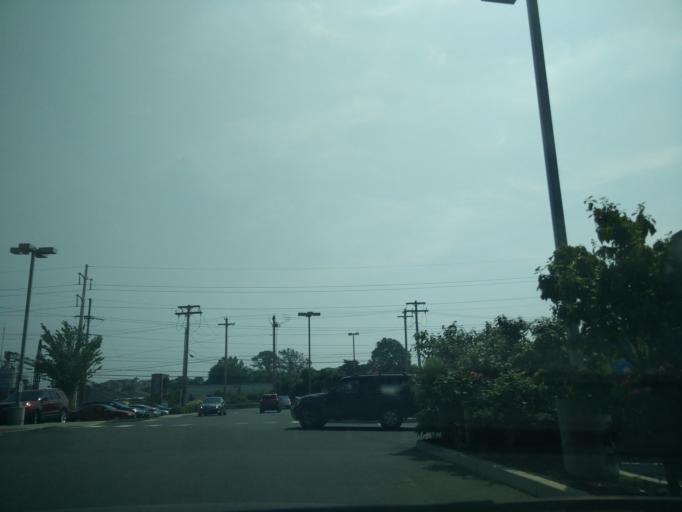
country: US
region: Connecticut
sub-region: Fairfield County
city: Fairfield
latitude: 41.1579
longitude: -73.2402
